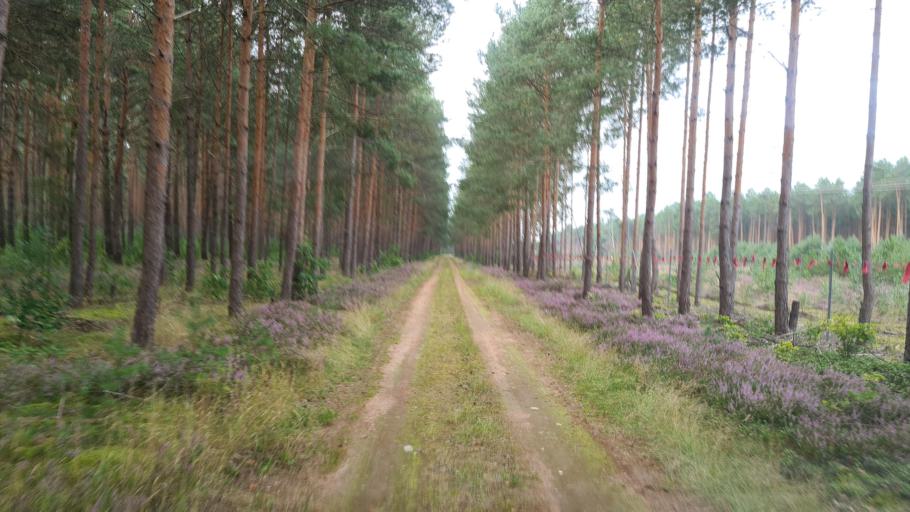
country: DE
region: Brandenburg
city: Hohenbucko
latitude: 51.7737
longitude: 13.5594
